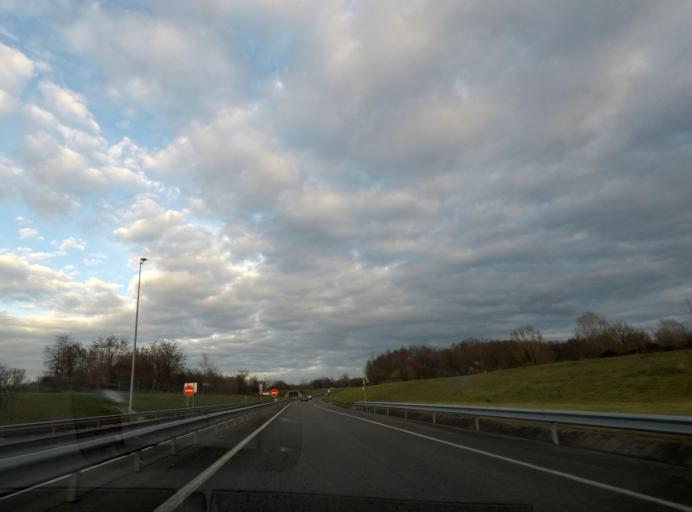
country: FR
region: Rhone-Alpes
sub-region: Departement de l'Ain
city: Crottet
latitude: 46.2960
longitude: 4.8994
